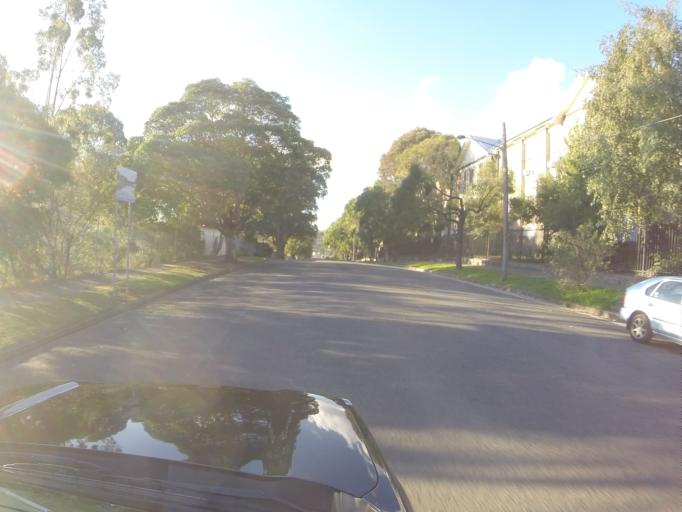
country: AU
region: New South Wales
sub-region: Canterbury
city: Canterbury
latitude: -33.9053
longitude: 151.1226
